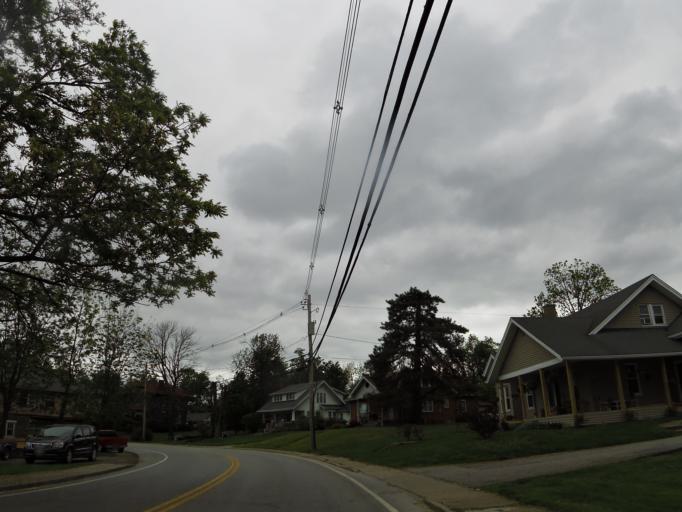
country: US
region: Kentucky
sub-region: Grant County
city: Williamstown
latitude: 38.6447
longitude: -84.5604
